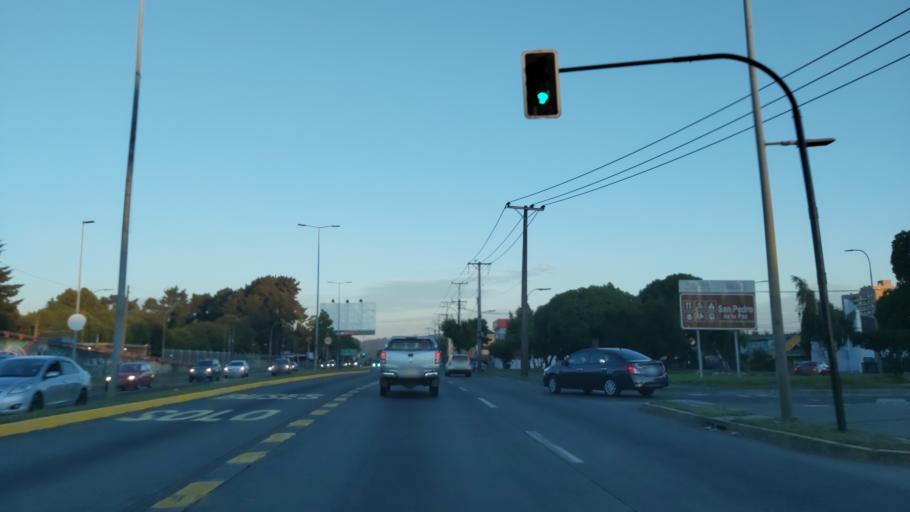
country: CL
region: Biobio
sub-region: Provincia de Concepcion
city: Concepcion
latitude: -36.8388
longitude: -73.0995
